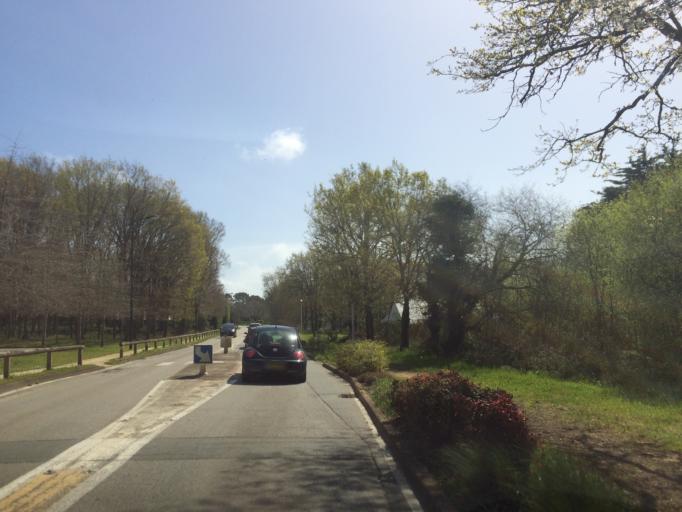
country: FR
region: Brittany
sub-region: Departement du Morbihan
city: La Trinite-sur-Mer
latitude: 47.5930
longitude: -3.0358
